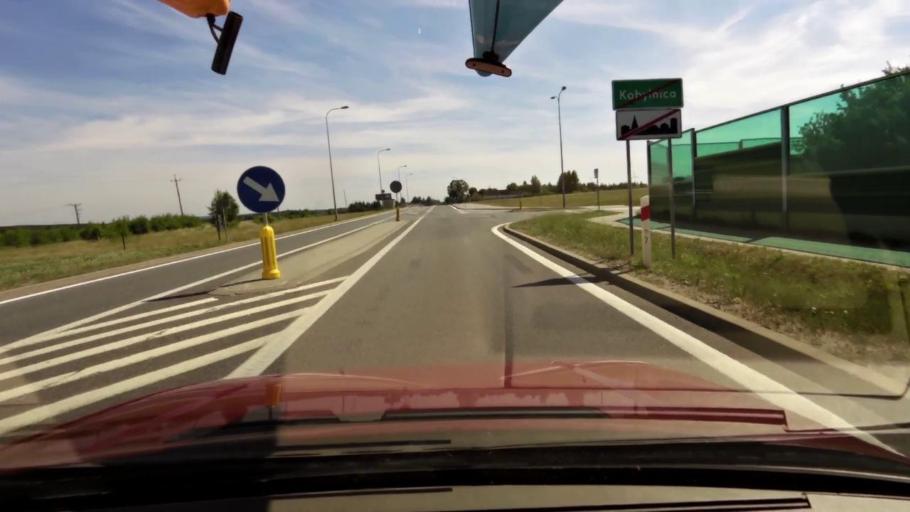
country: PL
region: Pomeranian Voivodeship
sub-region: Powiat slupski
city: Kobylnica
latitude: 54.4266
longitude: 17.0070
